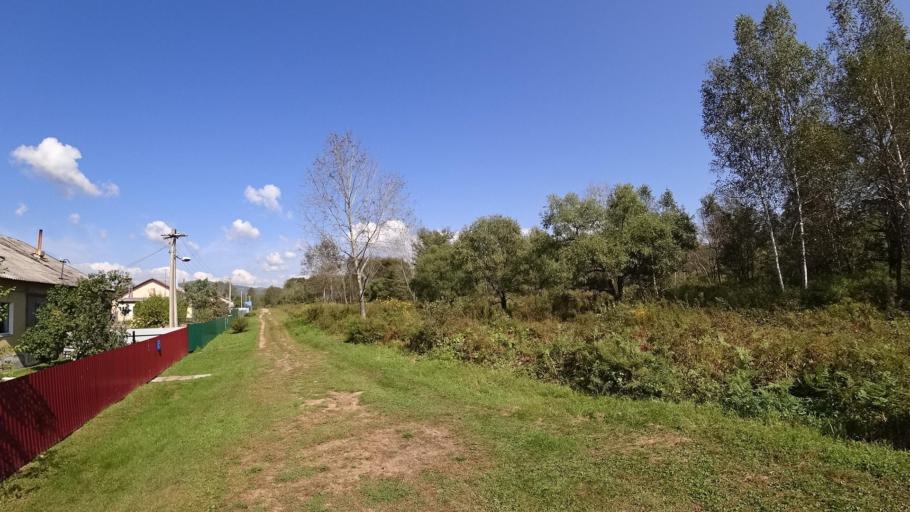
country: RU
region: Jewish Autonomous Oblast
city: Bira
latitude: 49.0113
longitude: 132.2331
